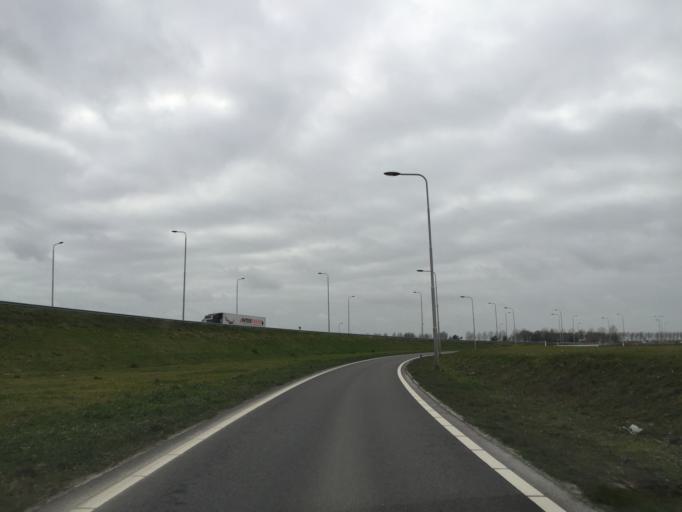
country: NL
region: North Holland
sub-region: Gemeente Aalsmeer
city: Aalsmeer
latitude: 52.2764
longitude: 4.7373
